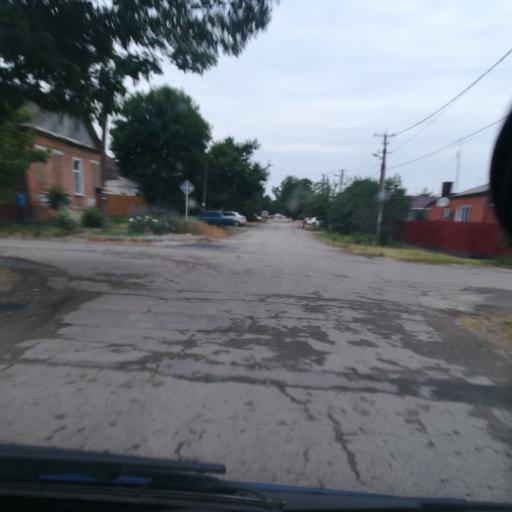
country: RU
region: Krasnodarskiy
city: Slavyansk-na-Kubani
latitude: 45.2626
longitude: 38.1265
